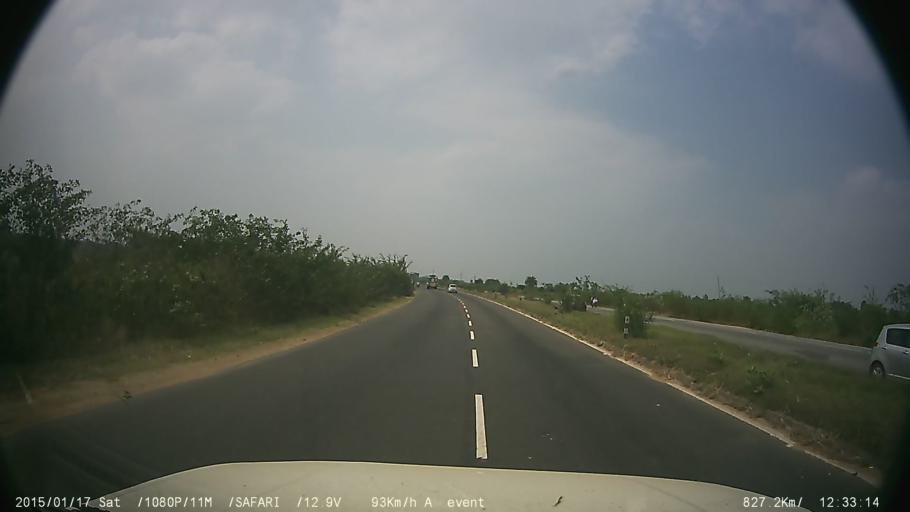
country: IN
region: Tamil Nadu
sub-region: Kancheepuram
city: Kanchipuram
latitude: 12.8721
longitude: 79.6372
